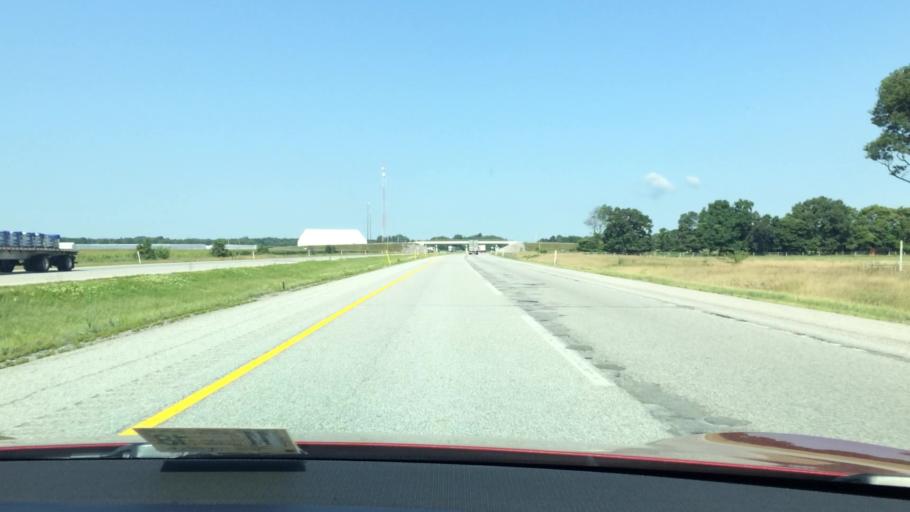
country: US
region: Michigan
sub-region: Saint Joseph County
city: White Pigeon
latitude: 41.7456
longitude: -85.5365
